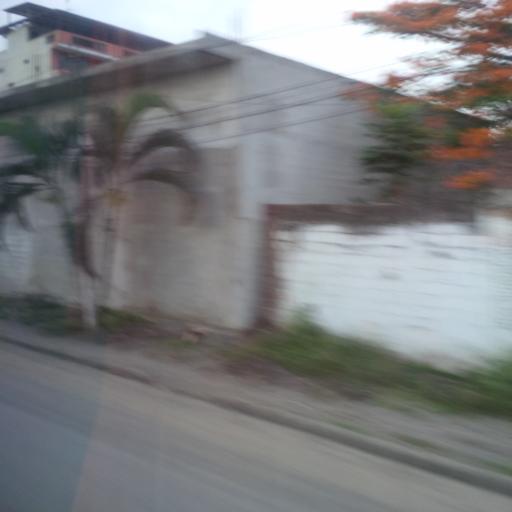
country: EC
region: Canar
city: La Troncal
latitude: -2.3338
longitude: -79.4003
